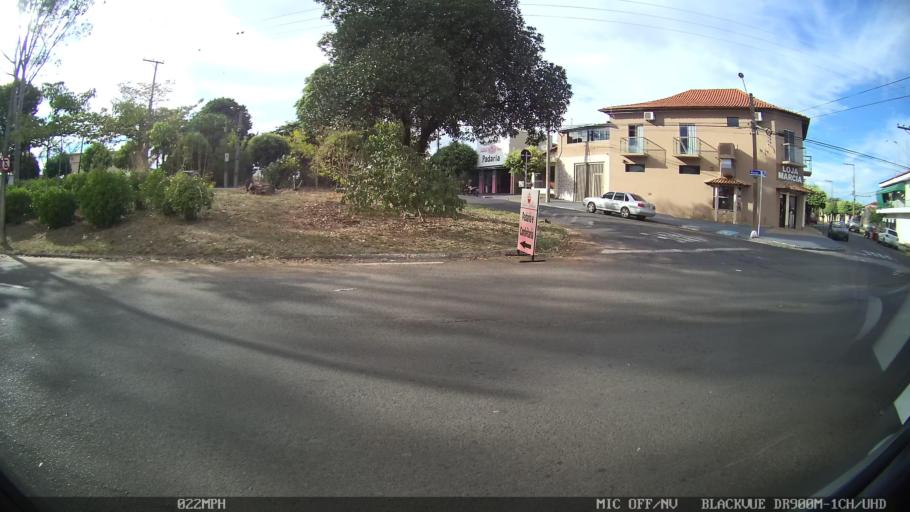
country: BR
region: Sao Paulo
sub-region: Catanduva
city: Catanduva
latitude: -21.1176
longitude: -48.9646
